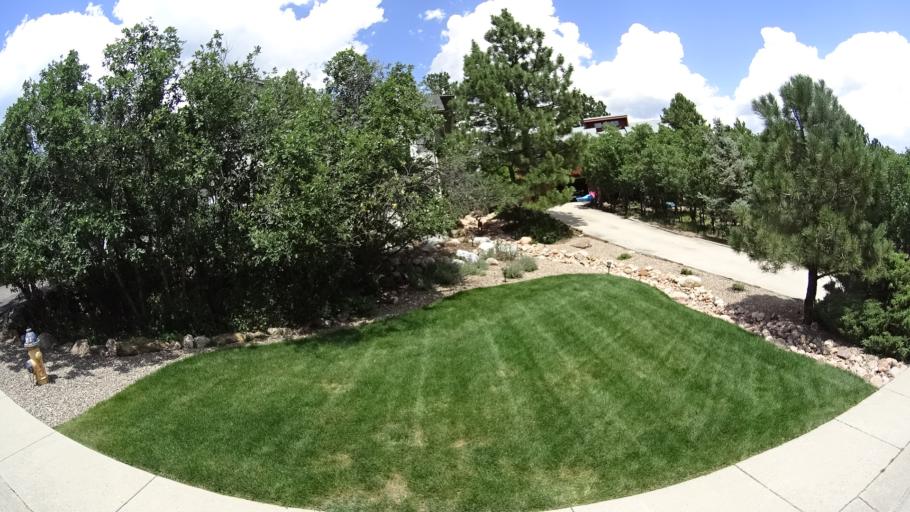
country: US
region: Colorado
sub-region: El Paso County
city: Air Force Academy
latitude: 38.9394
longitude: -104.8528
